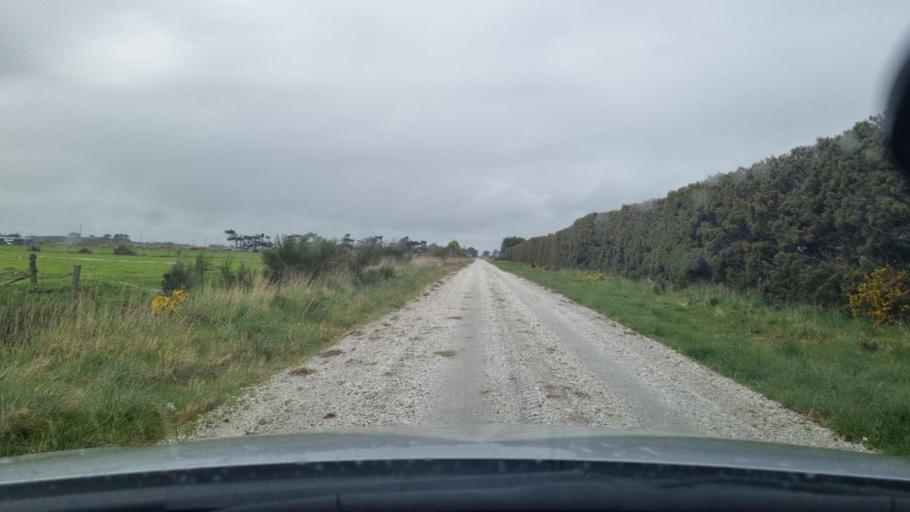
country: NZ
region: Southland
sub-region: Invercargill City
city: Invercargill
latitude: -46.4979
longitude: 168.4152
